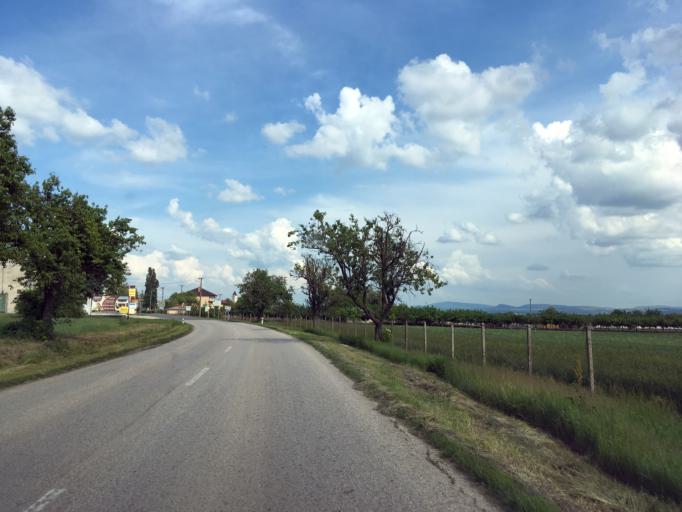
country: HU
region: Komarom-Esztergom
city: Almasfuzito
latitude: 47.7886
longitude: 18.2636
